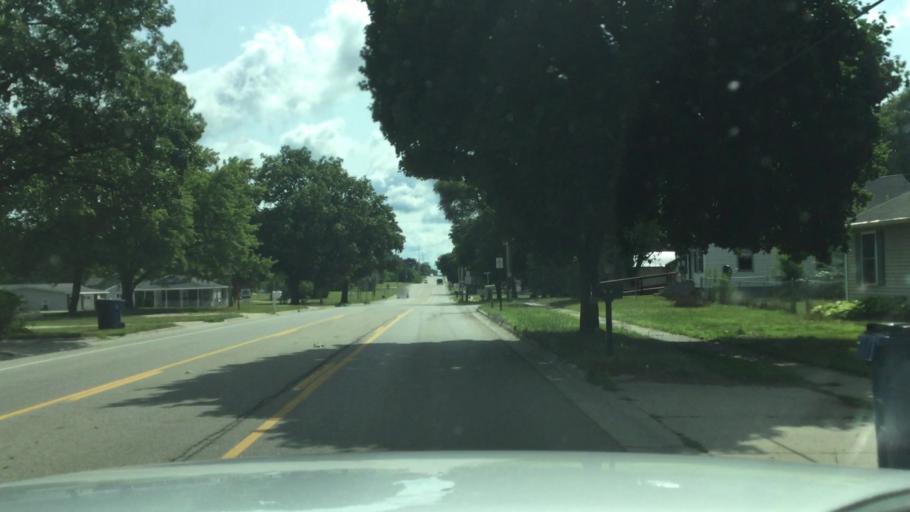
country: US
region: Michigan
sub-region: Montcalm County
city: Greenville
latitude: 43.1921
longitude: -85.2424
